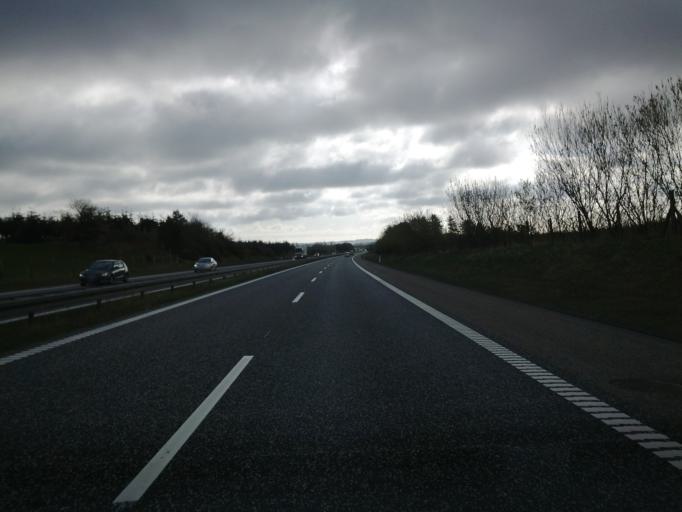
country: DK
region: North Denmark
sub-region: Bronderslev Kommune
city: Dronninglund
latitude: 57.2365
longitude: 10.2584
